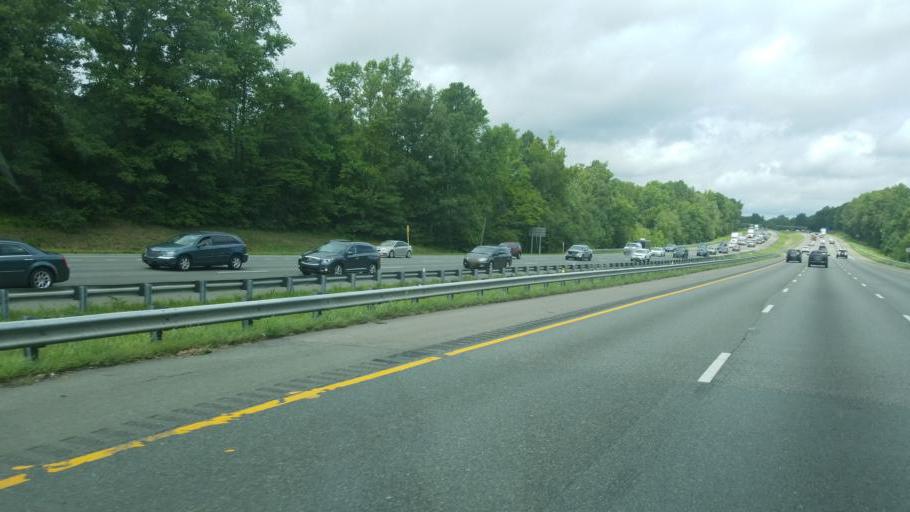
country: US
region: Virginia
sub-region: Caroline County
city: Bowling Green
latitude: 37.9854
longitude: -77.4926
